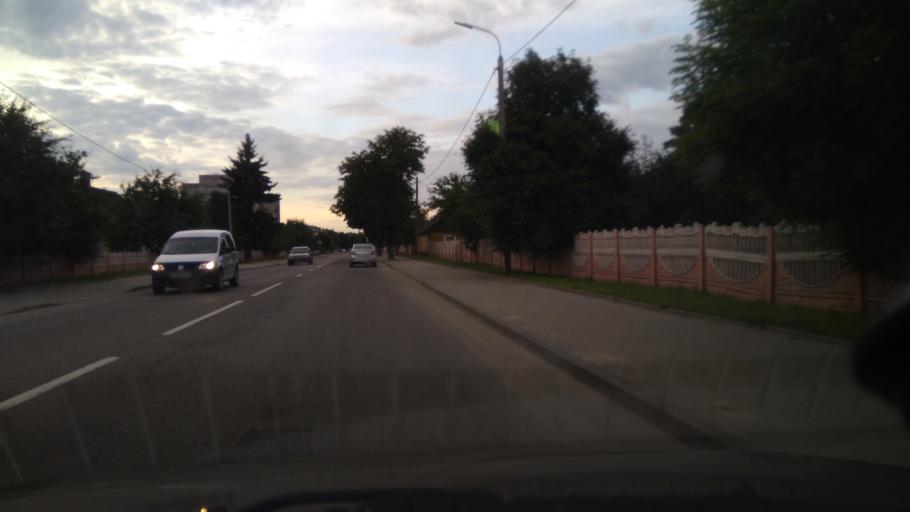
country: BY
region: Grodnenskaya
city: Shchuchin
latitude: 53.5988
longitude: 24.7431
